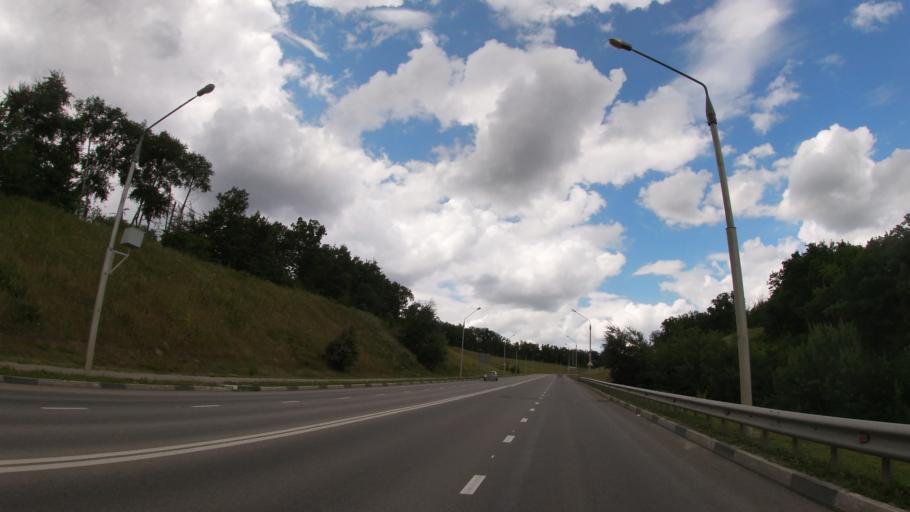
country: RU
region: Belgorod
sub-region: Belgorodskiy Rayon
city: Belgorod
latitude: 50.6214
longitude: 36.6149
